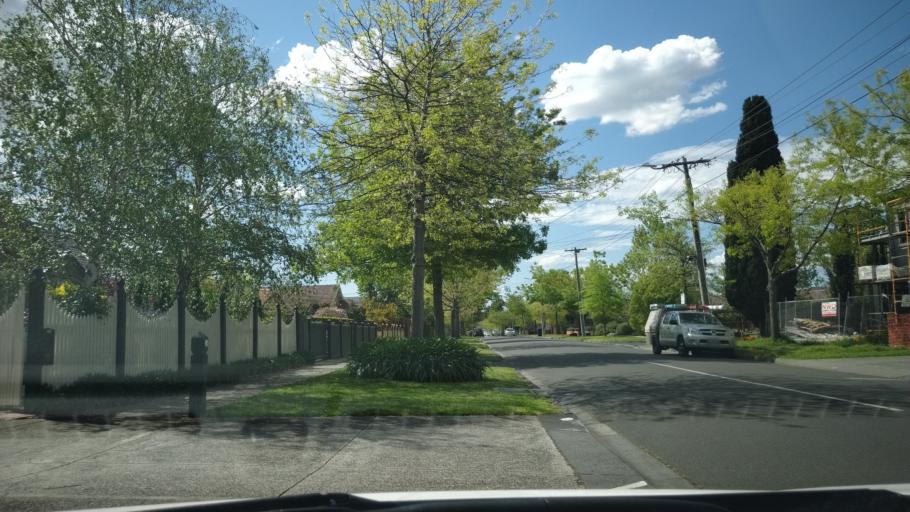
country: AU
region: Victoria
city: Carnegie
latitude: -37.8815
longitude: 145.0621
